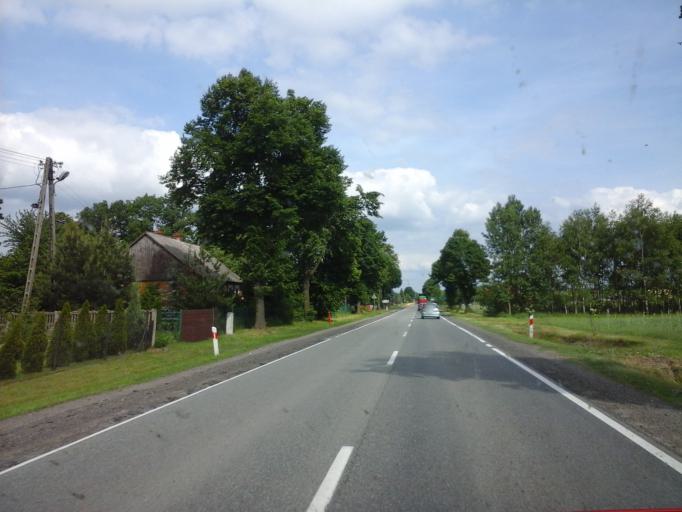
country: PL
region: Lodz Voivodeship
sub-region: Powiat opoczynski
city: Paradyz
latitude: 51.3081
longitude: 20.1013
